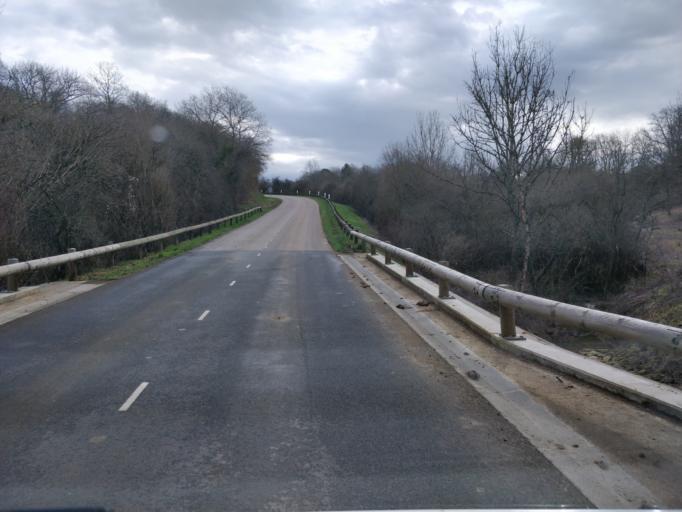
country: FR
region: Lorraine
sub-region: Departement de Meurthe-et-Moselle
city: Doncourt-les-Conflans
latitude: 49.1097
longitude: 5.9003
